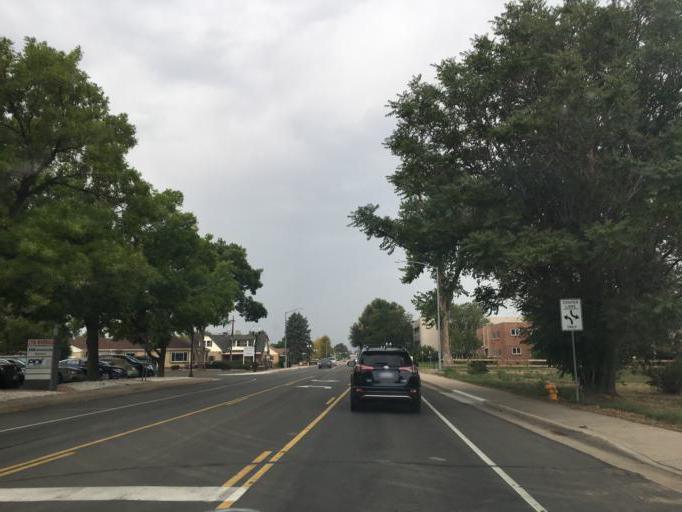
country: US
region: Colorado
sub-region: Jefferson County
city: Wheat Ridge
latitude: 39.7694
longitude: -105.0671
